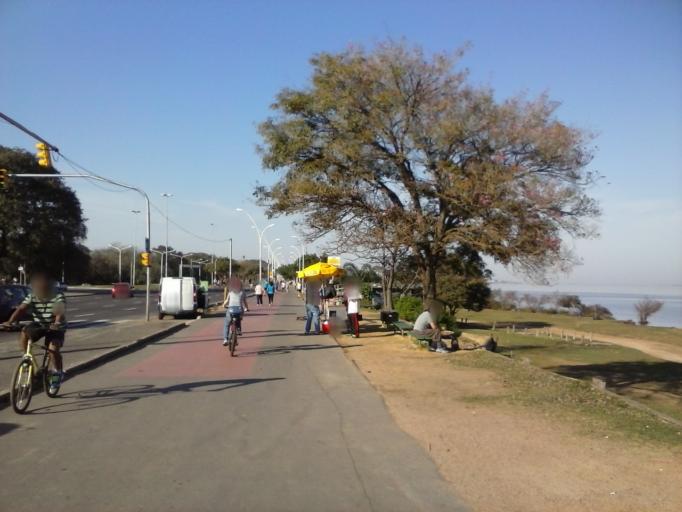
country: BR
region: Rio Grande do Sul
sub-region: Porto Alegre
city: Porto Alegre
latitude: -30.0361
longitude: -51.2415
